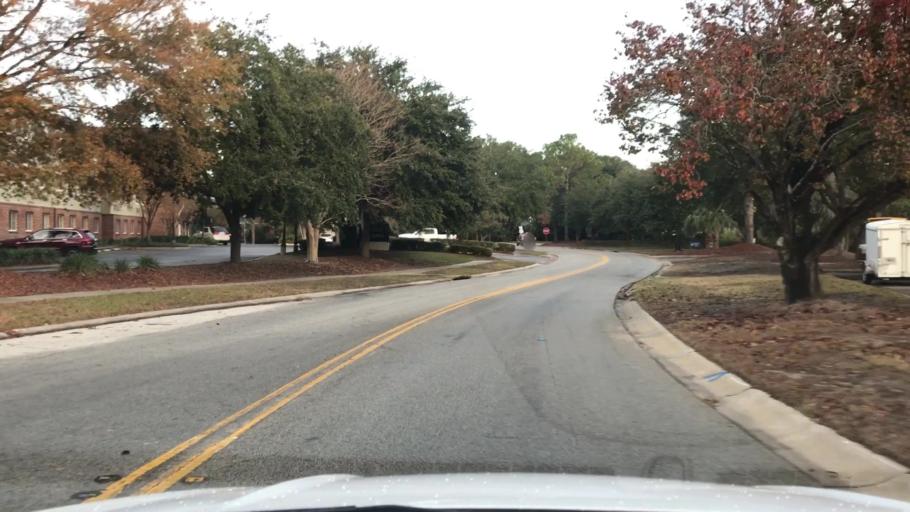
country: US
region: South Carolina
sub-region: Charleston County
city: Mount Pleasant
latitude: 32.8034
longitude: -79.8954
